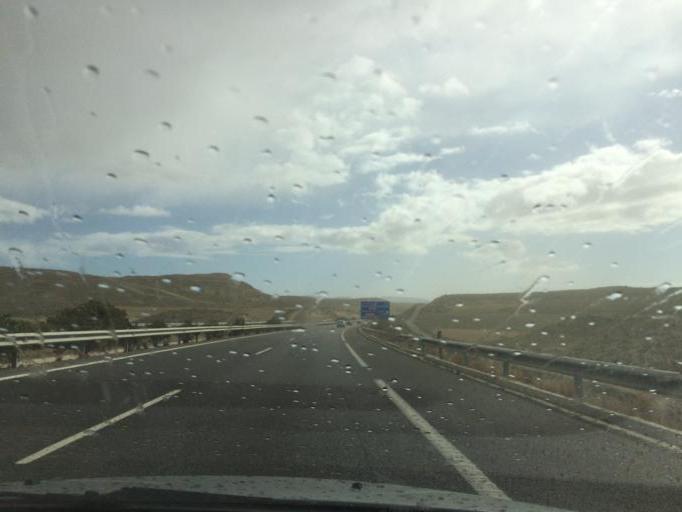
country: ES
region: Andalusia
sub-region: Provincia de Almeria
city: Retamar
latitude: 36.8714
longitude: -2.2822
